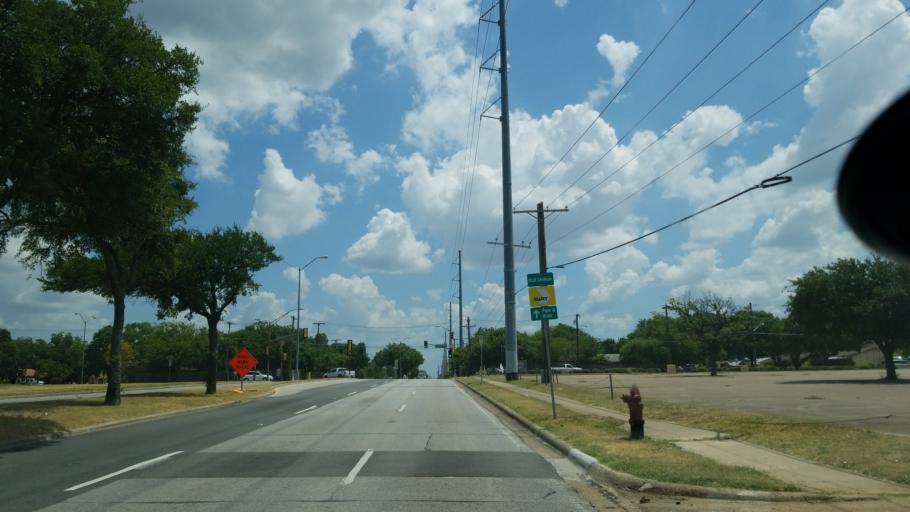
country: US
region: Texas
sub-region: Dallas County
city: Cockrell Hill
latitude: 32.7204
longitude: -96.9013
